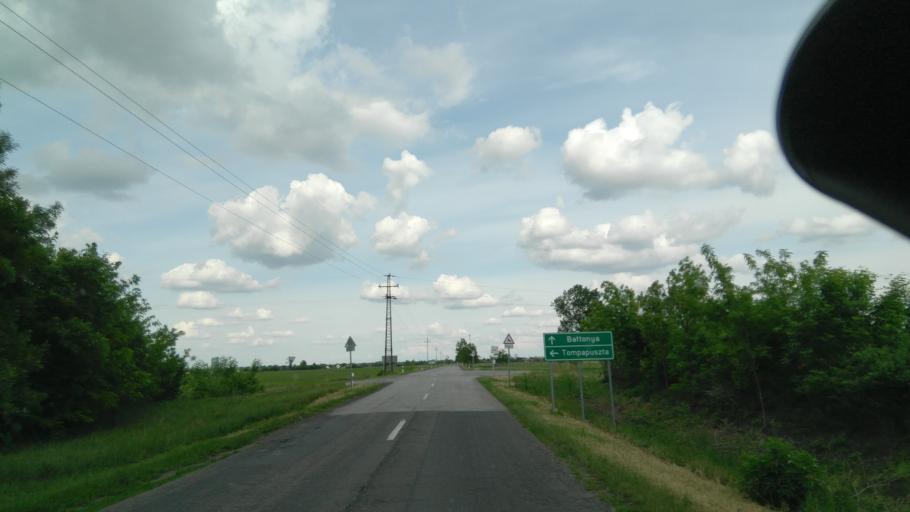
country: HU
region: Bekes
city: Battonya
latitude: 46.2930
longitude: 20.9855
